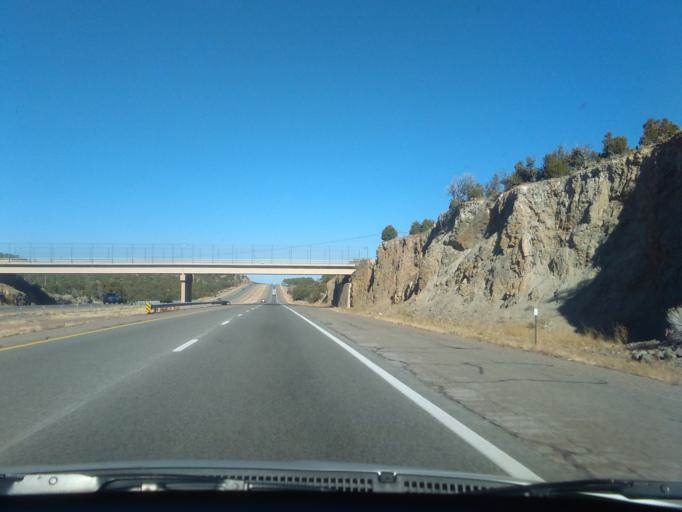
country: US
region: New Mexico
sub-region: Santa Fe County
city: Eldorado at Santa Fe
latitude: 35.6048
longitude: -105.9115
